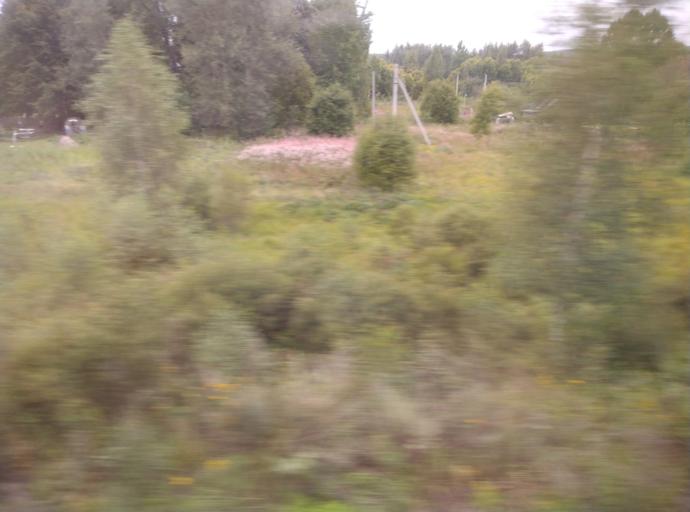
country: RU
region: Kostroma
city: Kosmynino
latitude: 57.5959
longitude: 40.7739
